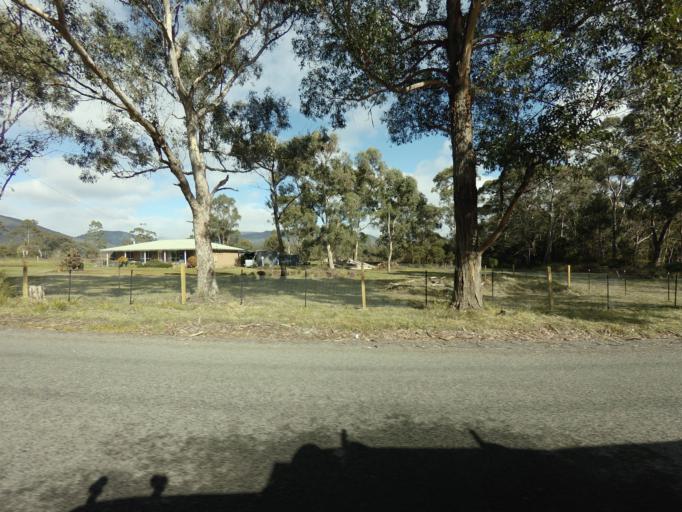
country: AU
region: Tasmania
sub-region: Huon Valley
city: Geeveston
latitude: -43.4360
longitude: 146.9037
